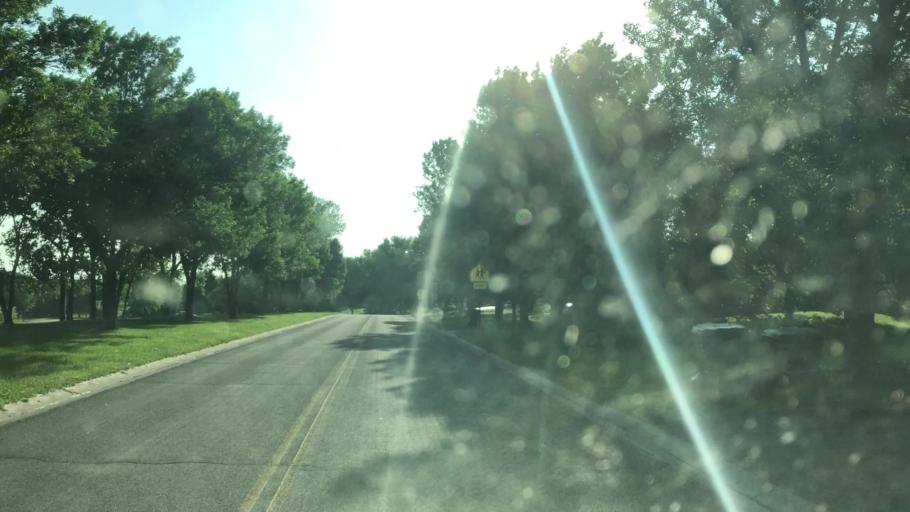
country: US
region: New York
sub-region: Wayne County
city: Macedon
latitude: 43.1222
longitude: -77.3086
